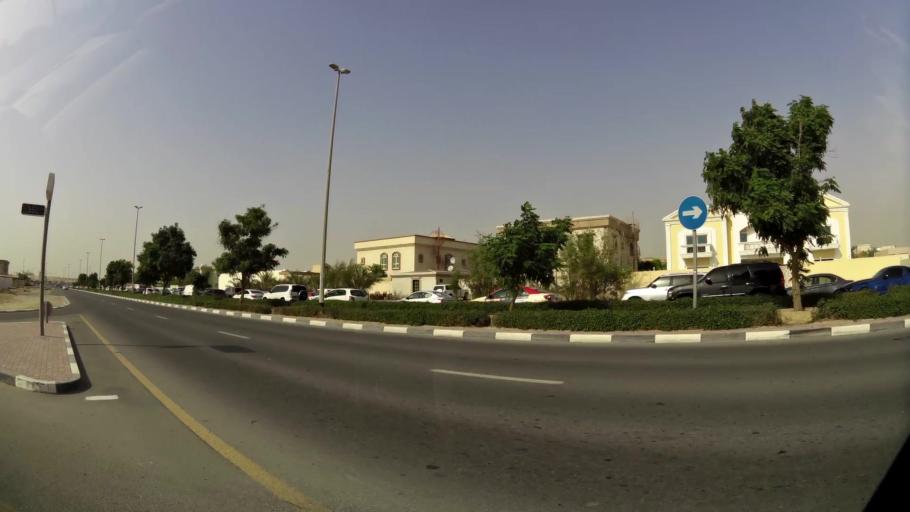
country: AE
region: Ash Shariqah
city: Sharjah
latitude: 25.2517
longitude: 55.4303
